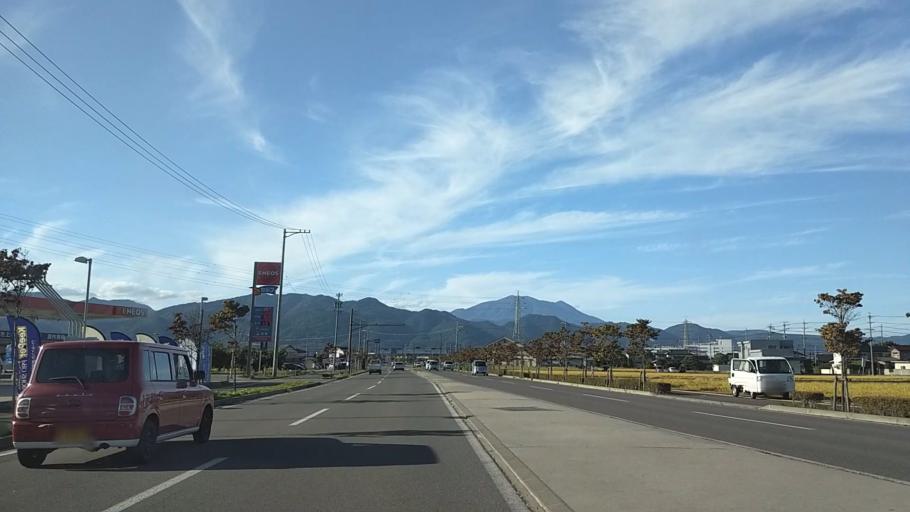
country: JP
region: Nagano
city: Nagano-shi
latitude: 36.5986
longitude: 138.1814
